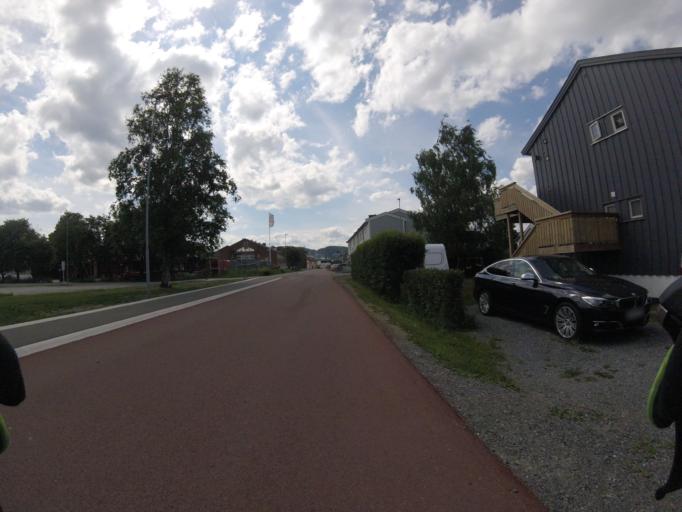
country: NO
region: Akershus
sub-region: Skedsmo
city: Lillestrom
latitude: 59.9619
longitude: 11.0462
